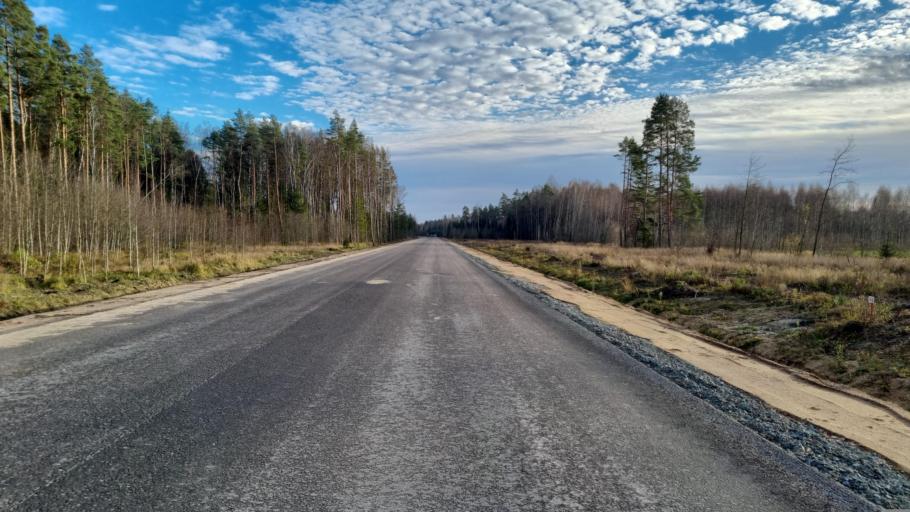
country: LV
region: Kekava
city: Kekava
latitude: 56.7997
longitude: 24.2055
